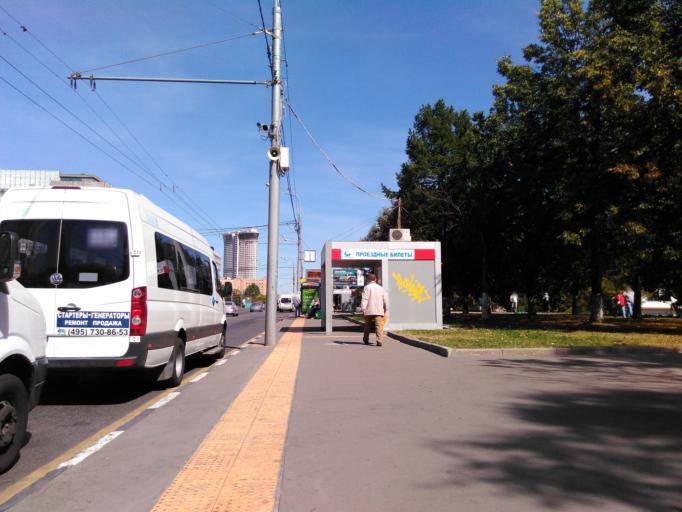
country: RU
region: Moskovskaya
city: Cheremushki
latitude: 55.6570
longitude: 37.5406
